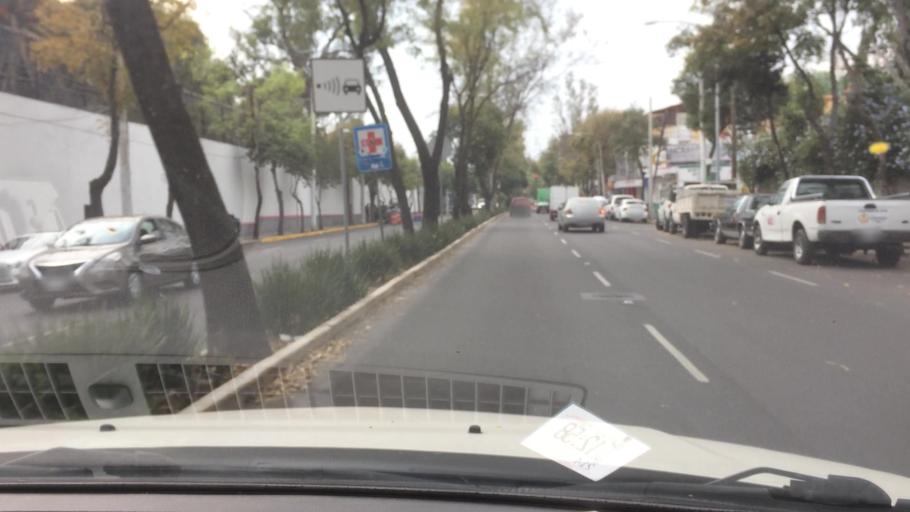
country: MX
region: Mexico City
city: Tlalpan
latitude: 19.2927
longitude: -99.1686
